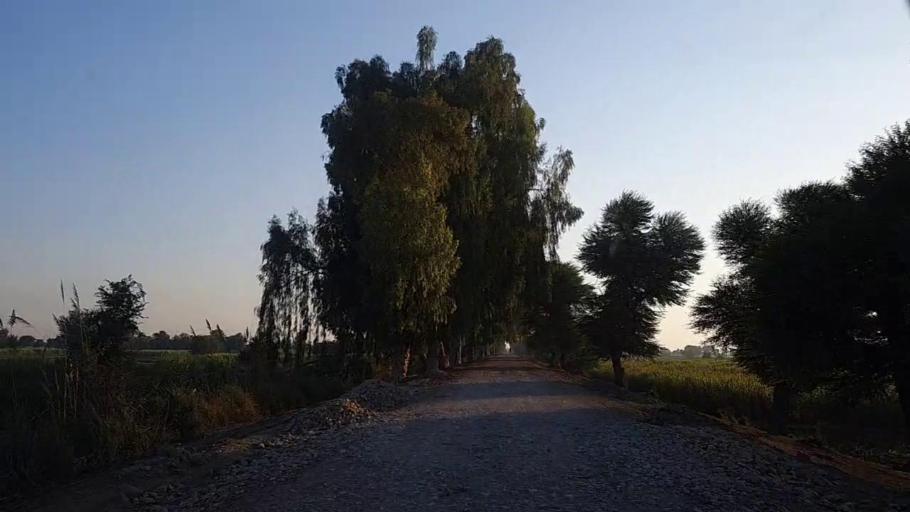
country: PK
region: Sindh
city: Sobhadero
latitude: 27.3825
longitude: 68.3813
